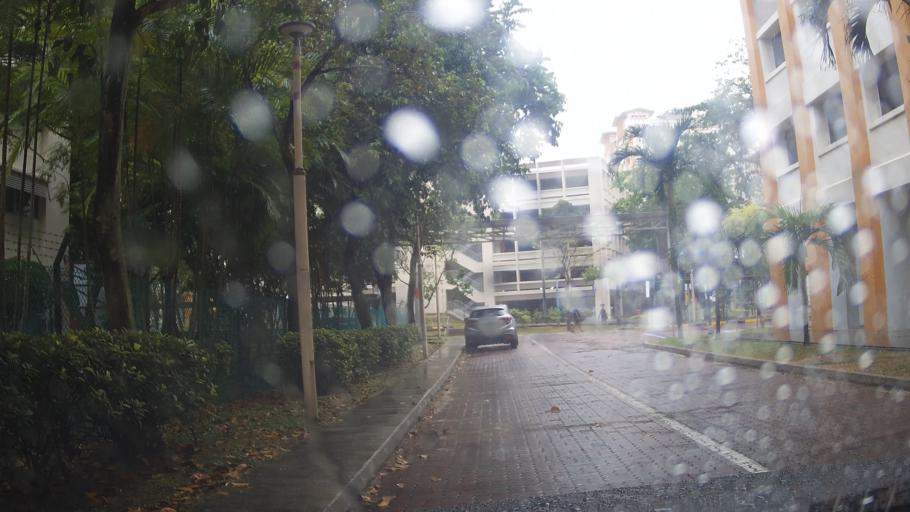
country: MY
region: Johor
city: Johor Bahru
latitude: 1.4432
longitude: 103.8000
